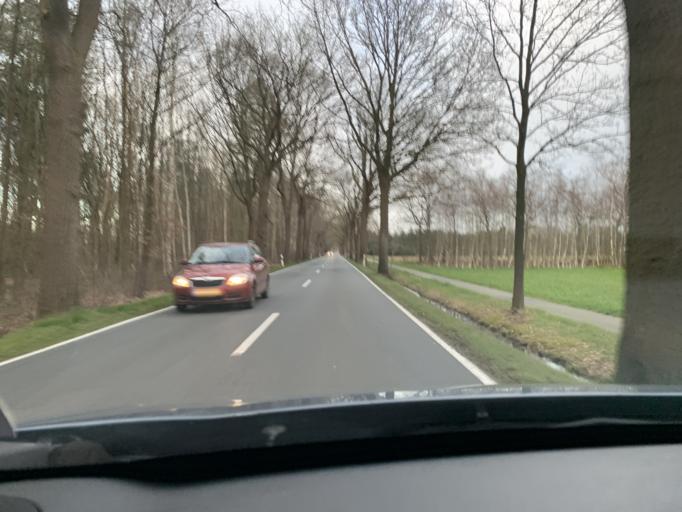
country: DE
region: Lower Saxony
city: Apen
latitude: 53.1783
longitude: 7.8329
